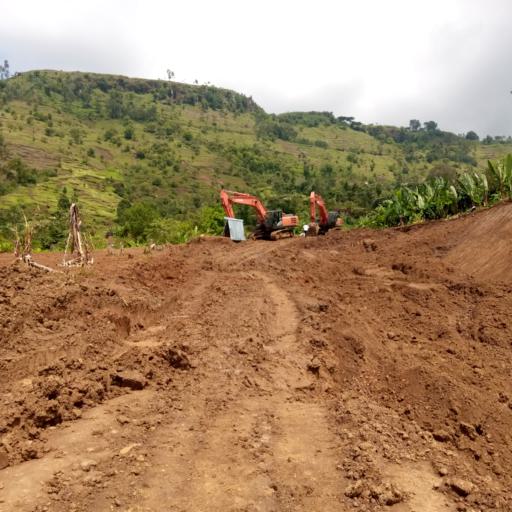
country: ET
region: Southern Nations, Nationalities, and People's Region
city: Arba Minch'
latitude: 6.3161
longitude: 37.3593
